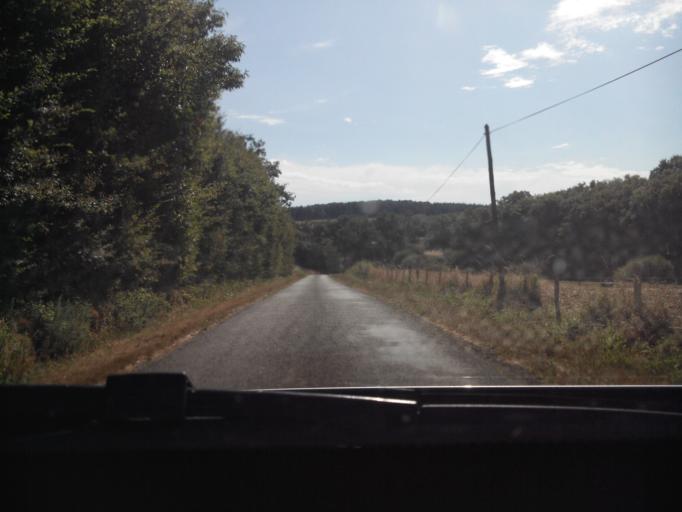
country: FR
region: Poitou-Charentes
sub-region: Departement de la Charente
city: Etagnac
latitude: 45.9351
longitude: 0.7701
